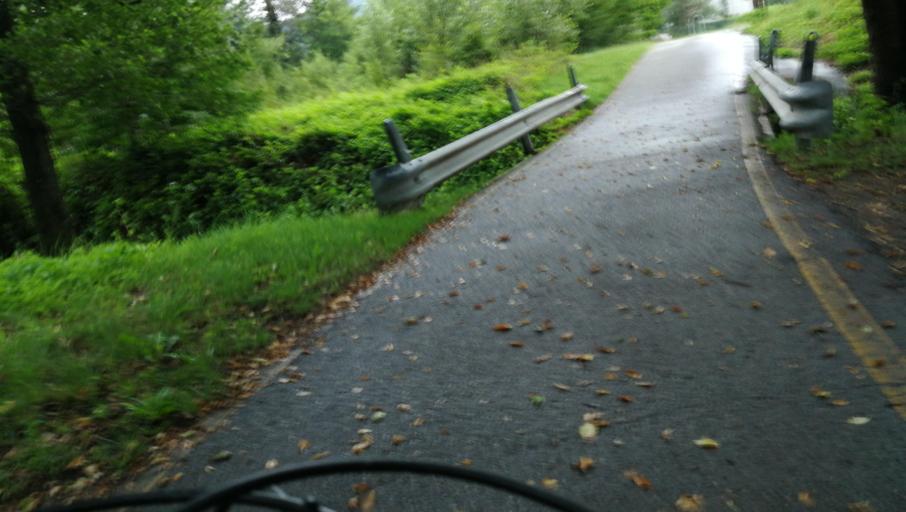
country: IT
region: Lombardy
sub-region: Provincia di Varese
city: Laveno
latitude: 45.9033
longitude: 8.6292
